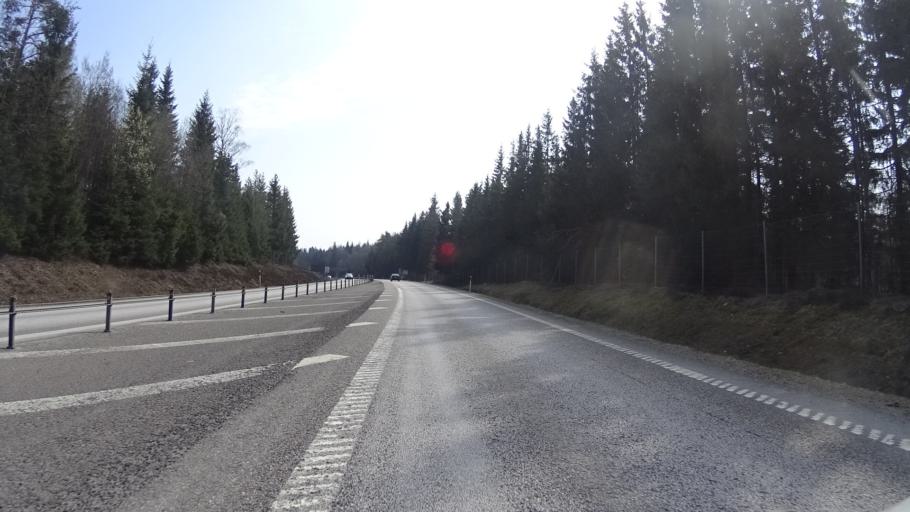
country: SE
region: Joenkoeping
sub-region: Mullsjo Kommun
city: Mullsjoe
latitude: 57.7665
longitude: 13.7238
